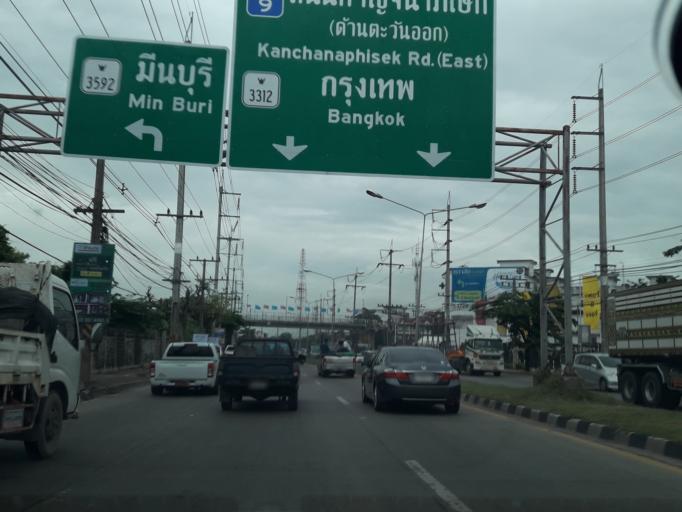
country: TH
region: Pathum Thani
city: Lam Luk Ka
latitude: 13.9372
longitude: 100.7529
